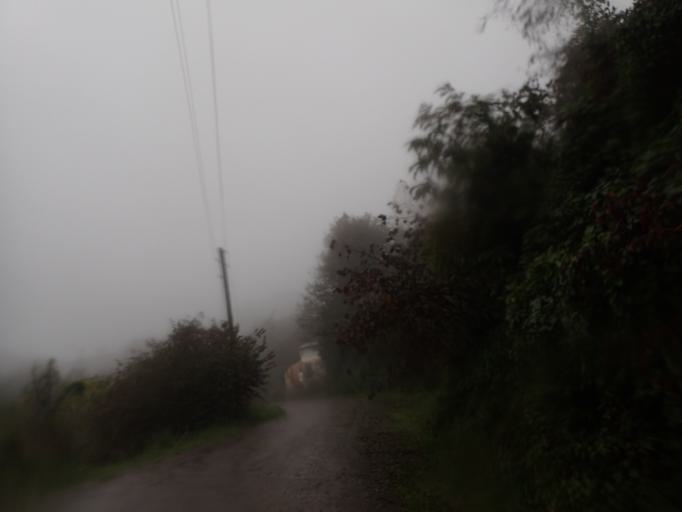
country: TR
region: Ordu
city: Persembe
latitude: 41.0255
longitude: 37.7194
